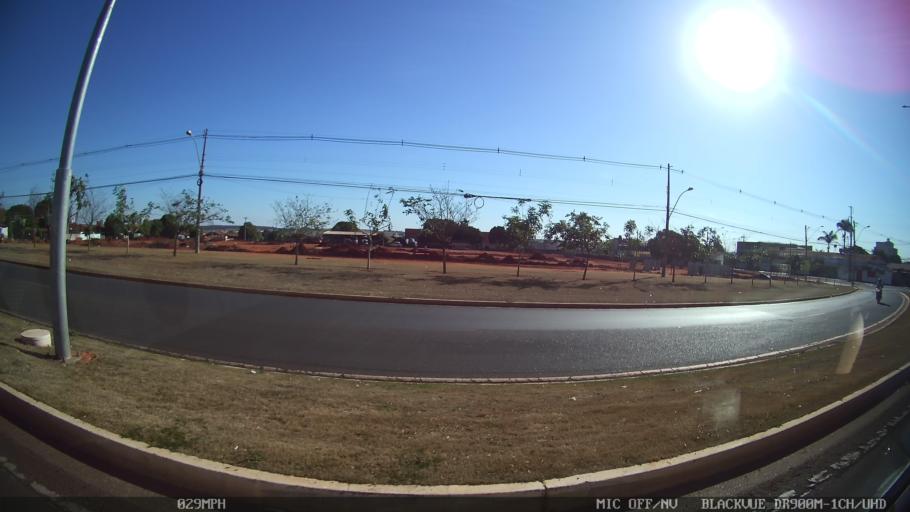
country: BR
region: Sao Paulo
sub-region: Olimpia
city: Olimpia
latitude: -20.7243
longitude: -48.9057
